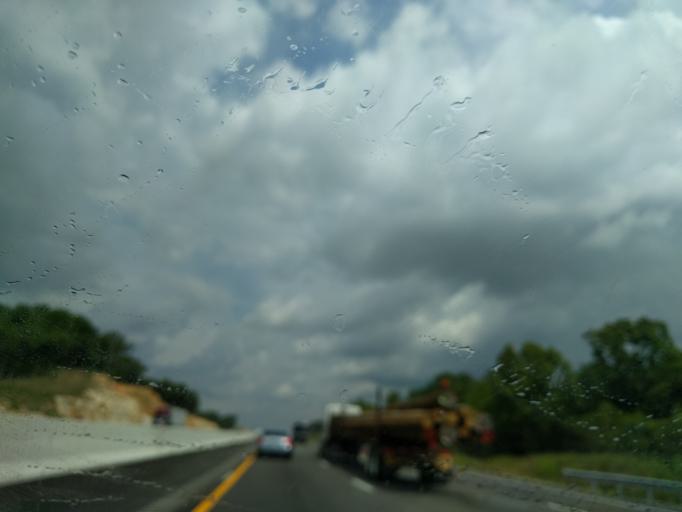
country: US
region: Kentucky
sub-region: Hart County
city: Munfordville
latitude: 37.4165
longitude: -85.8820
